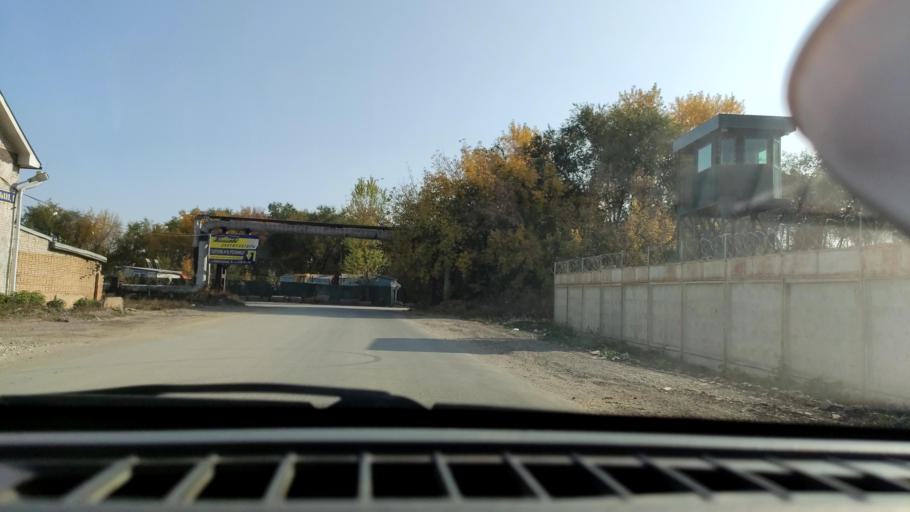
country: RU
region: Samara
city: Samara
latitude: 53.1908
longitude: 50.2659
